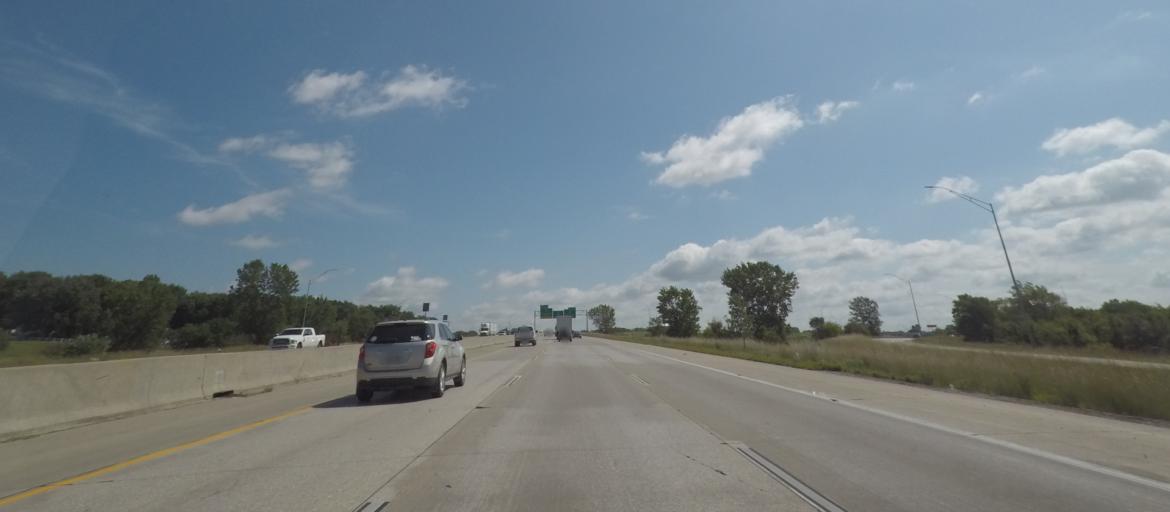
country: US
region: Iowa
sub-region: Polk County
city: Saylorville
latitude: 41.6492
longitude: -93.6065
